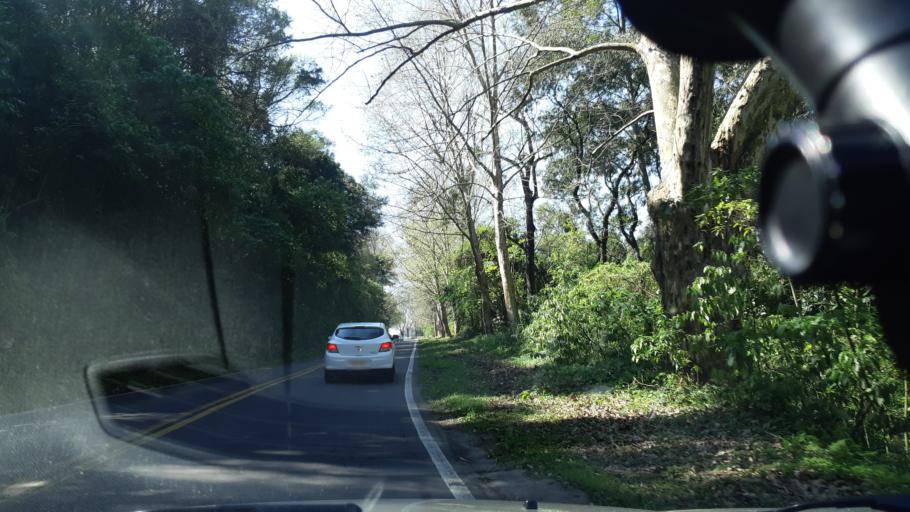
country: BR
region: Rio Grande do Sul
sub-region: Nova Petropolis
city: Nova Petropolis
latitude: -29.4047
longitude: -51.1289
